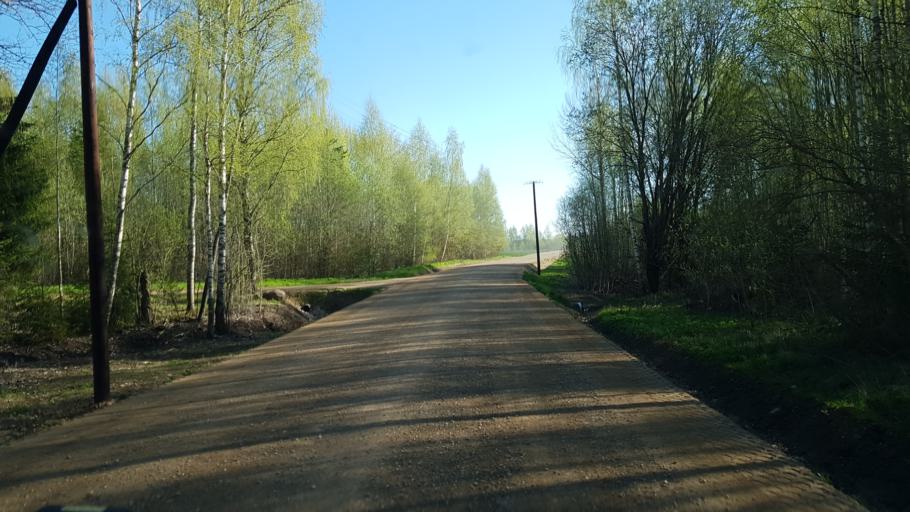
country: EE
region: Polvamaa
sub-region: Polva linn
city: Polva
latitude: 58.1205
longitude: 27.2393
